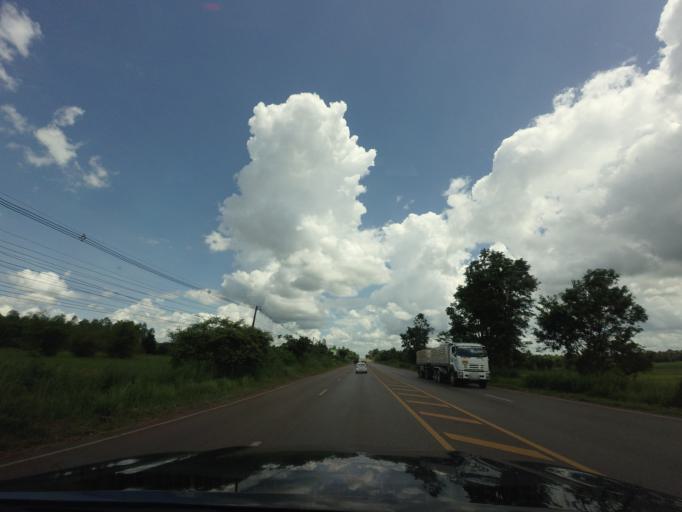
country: TH
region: Changwat Udon Thani
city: Ban Dung
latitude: 17.6853
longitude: 103.2066
